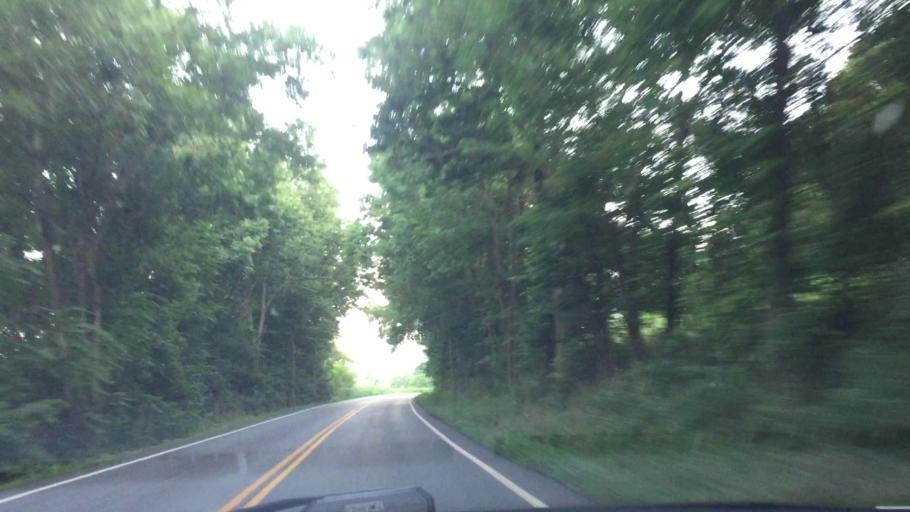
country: US
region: Kentucky
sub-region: Carroll County
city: Carrollton
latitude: 38.6373
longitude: -85.1404
